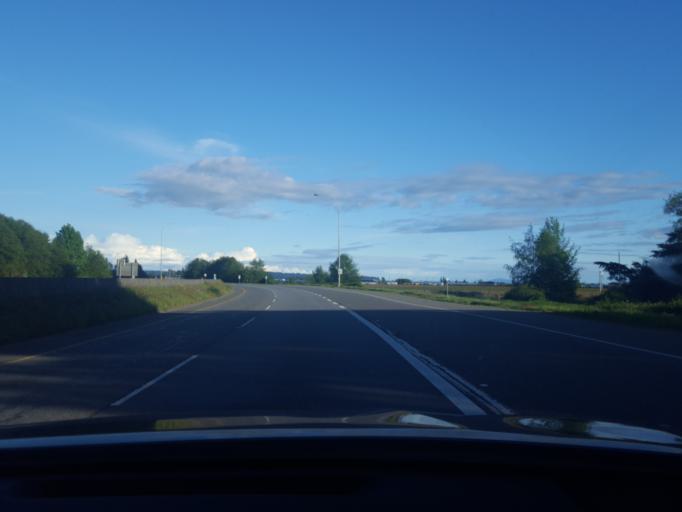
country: CA
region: British Columbia
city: Delta
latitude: 49.1194
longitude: -122.9270
